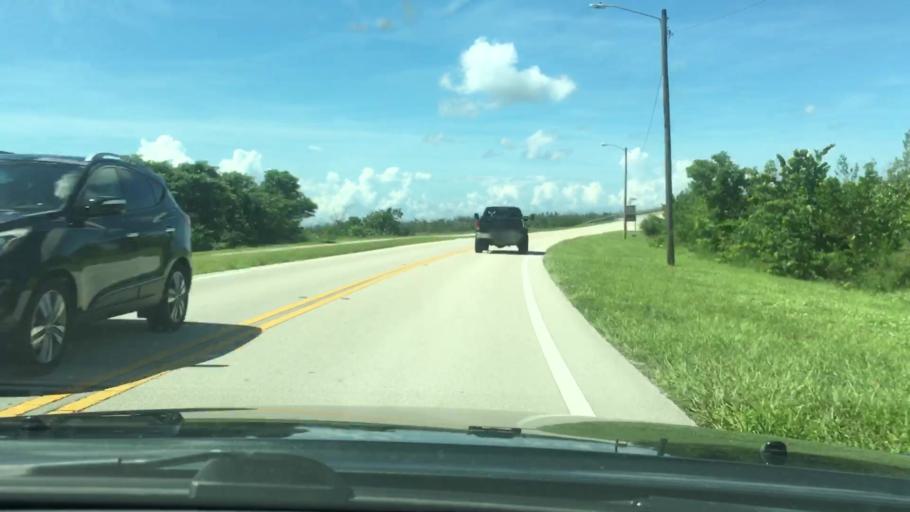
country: US
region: Florida
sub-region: Collier County
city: Marco
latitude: 25.9344
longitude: -81.6490
